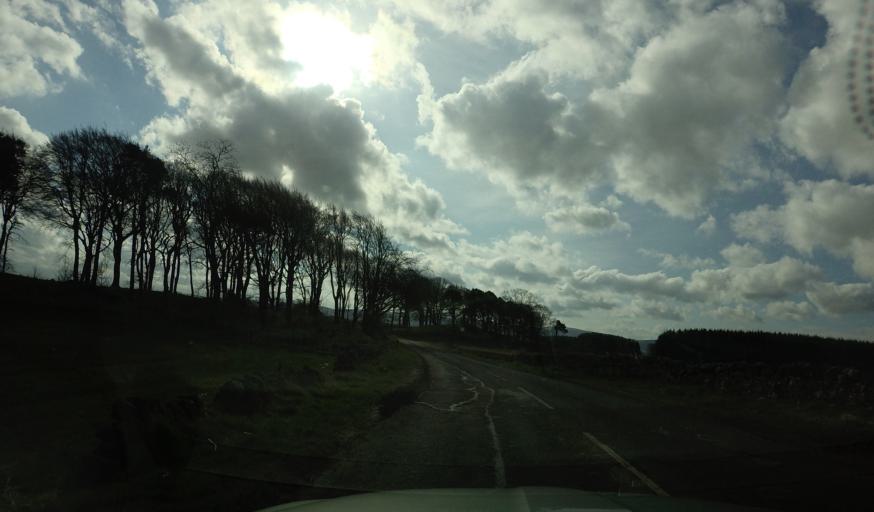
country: GB
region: Scotland
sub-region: Midlothian
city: Penicuik
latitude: 55.8023
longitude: -3.1719
